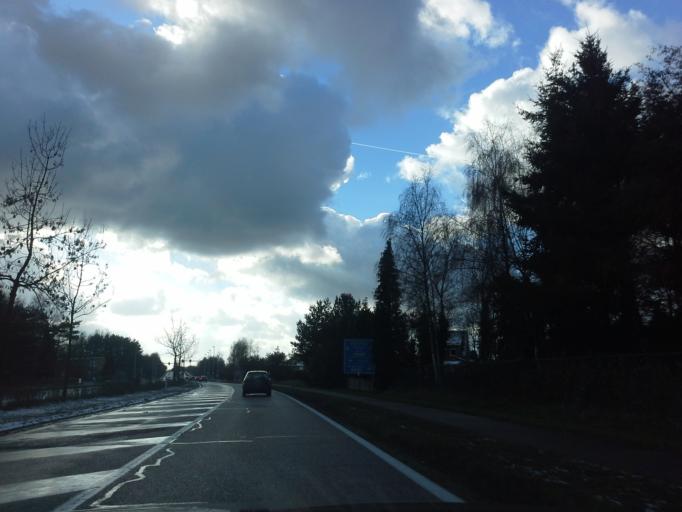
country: BE
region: Flanders
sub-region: Provincie Antwerpen
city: Mol
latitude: 51.2022
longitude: 5.1471
